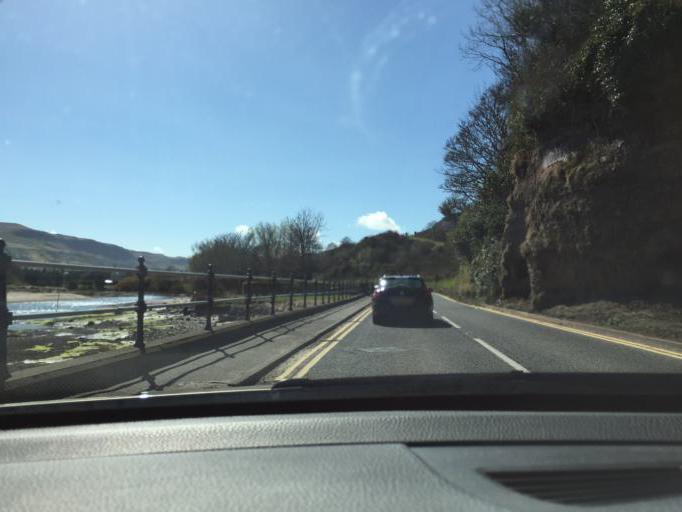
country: GB
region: Northern Ireland
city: Glenariff
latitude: 55.0643
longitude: -6.0585
